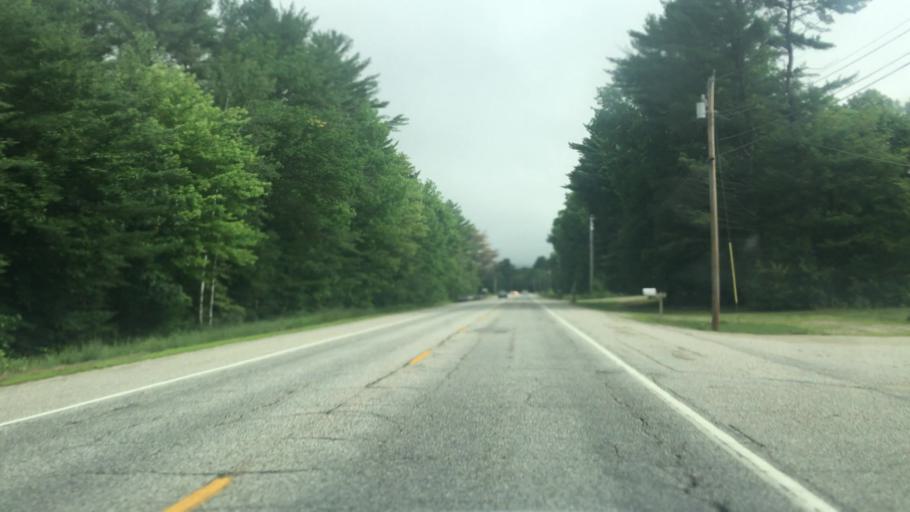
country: US
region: Maine
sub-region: Oxford County
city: Paris
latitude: 44.2689
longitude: -70.5146
